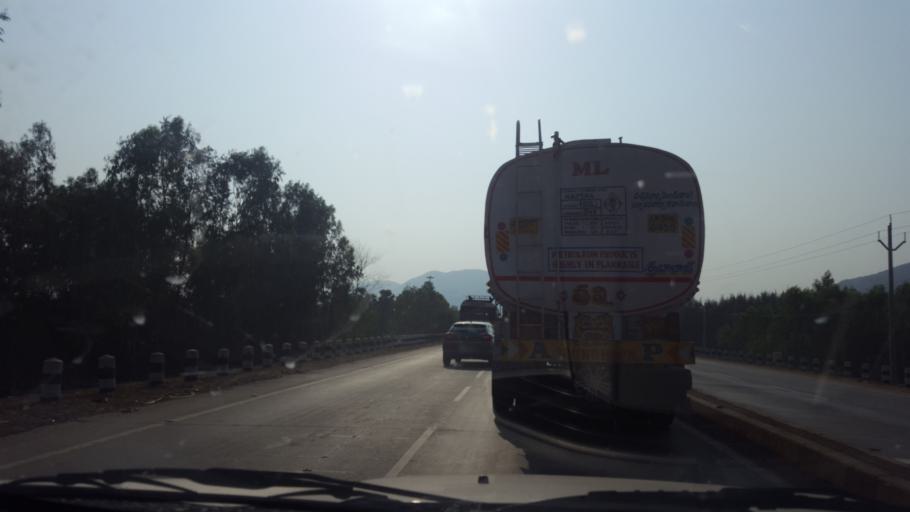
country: IN
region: Andhra Pradesh
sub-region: Vishakhapatnam
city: Anakapalle
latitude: 17.6475
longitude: 82.9118
